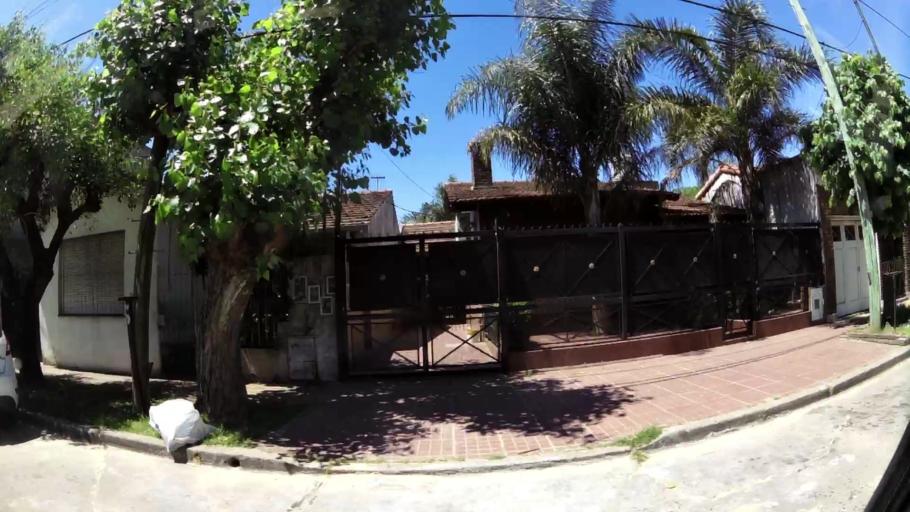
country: AR
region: Buenos Aires
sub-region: Partido de San Isidro
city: San Isidro
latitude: -34.5053
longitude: -58.5329
